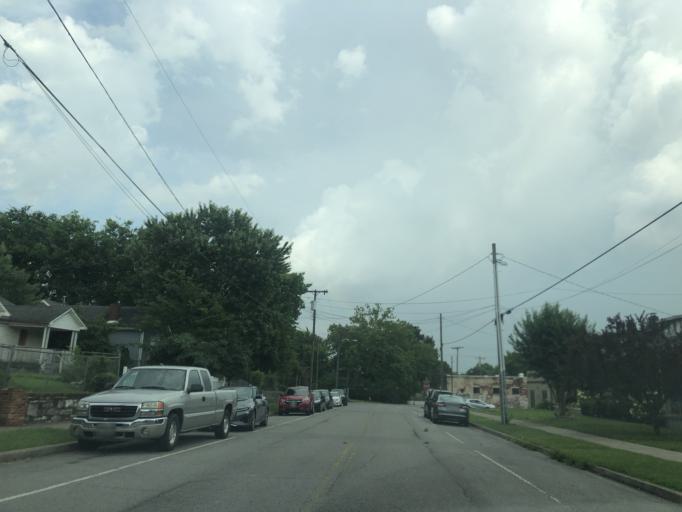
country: US
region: Tennessee
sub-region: Davidson County
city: Nashville
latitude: 36.1846
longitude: -86.7944
